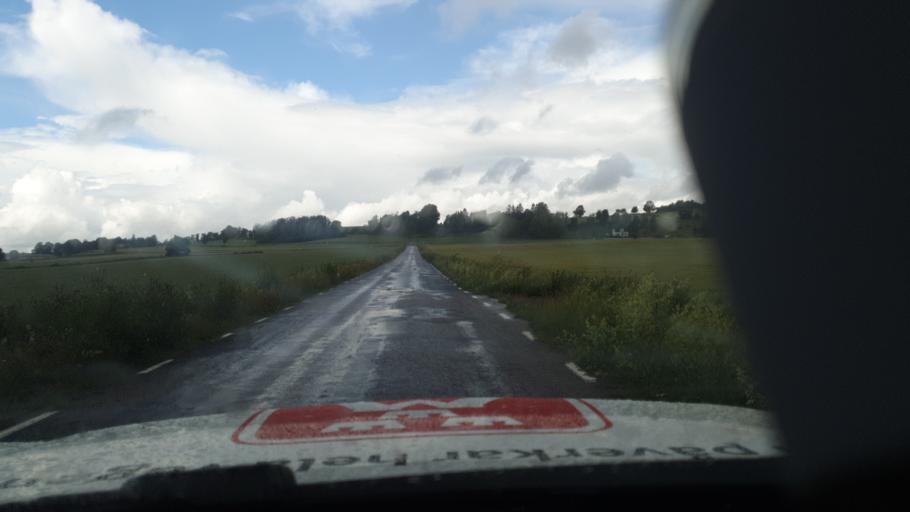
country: SE
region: Vaestra Goetaland
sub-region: Falkopings Kommun
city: Akarp
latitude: 58.1191
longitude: 13.7745
